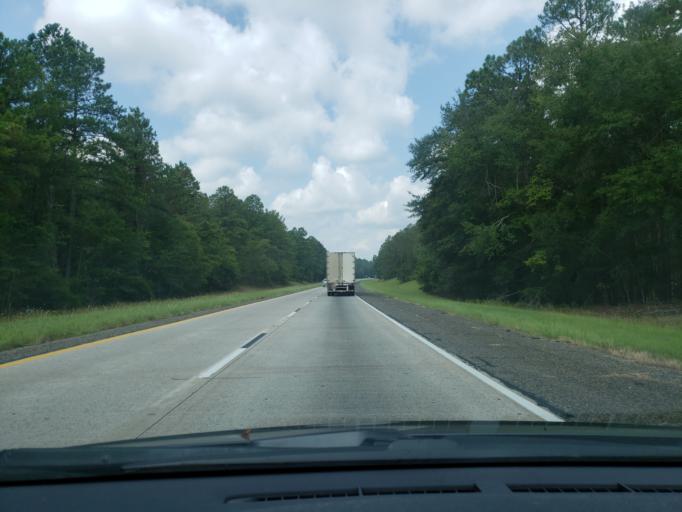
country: US
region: Georgia
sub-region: Treutlen County
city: Soperton
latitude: 32.4266
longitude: -82.5427
